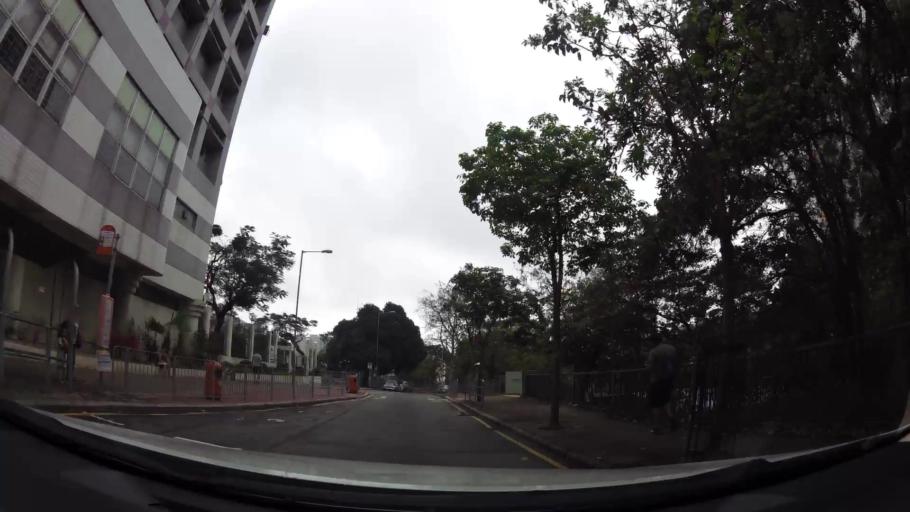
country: HK
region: Central and Western
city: Central
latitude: 22.2499
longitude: 114.1590
